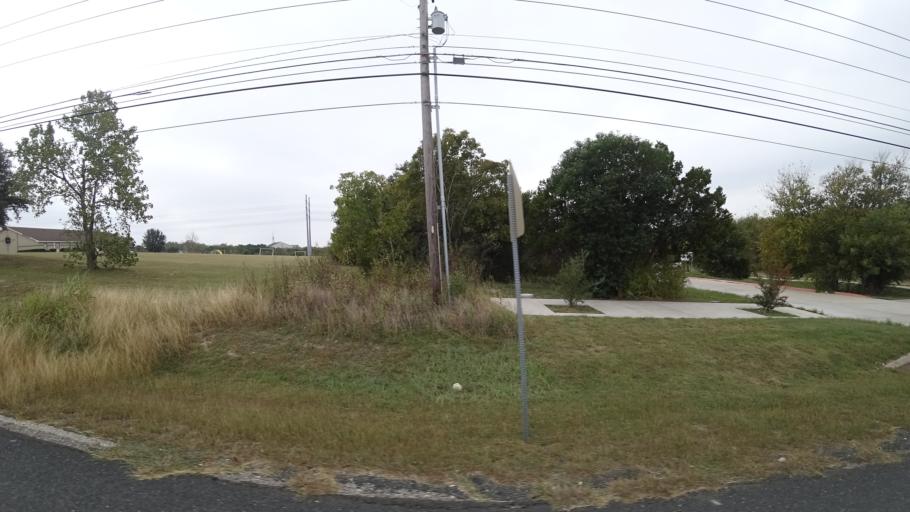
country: US
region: Texas
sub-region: Travis County
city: Pflugerville
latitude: 30.3881
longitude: -97.6536
